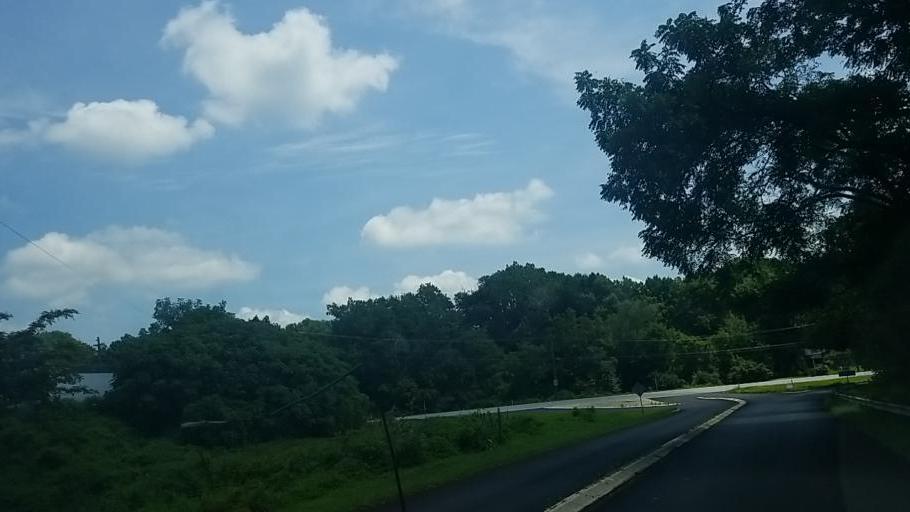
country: US
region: Delaware
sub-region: New Castle County
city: Hockessin
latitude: 39.7982
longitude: -75.7264
